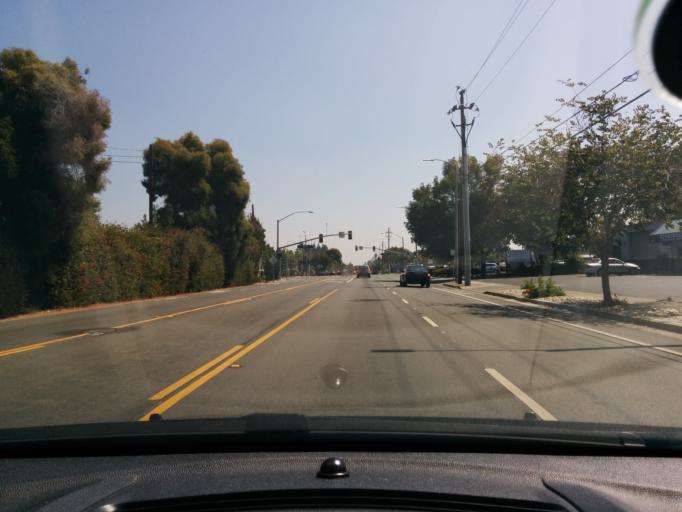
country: US
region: California
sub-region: Santa Clara County
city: Sunnyvale
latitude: 37.3834
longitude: -122.0459
